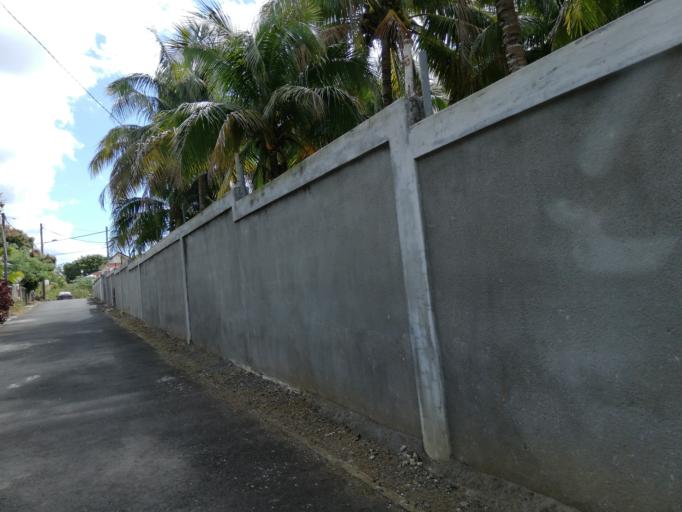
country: MU
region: Moka
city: Moka
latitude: -20.2200
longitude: 57.4762
